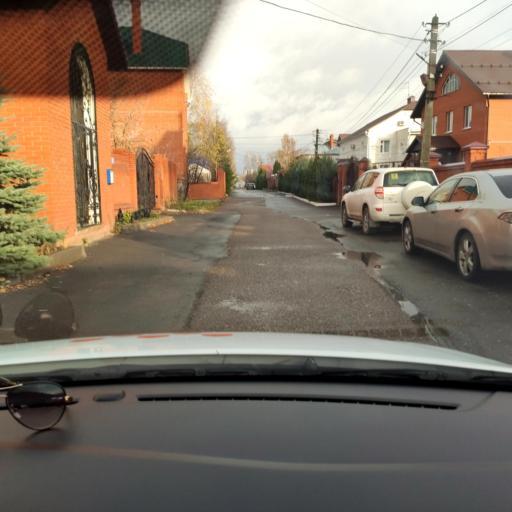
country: RU
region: Tatarstan
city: Stolbishchi
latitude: 55.7443
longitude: 49.2422
